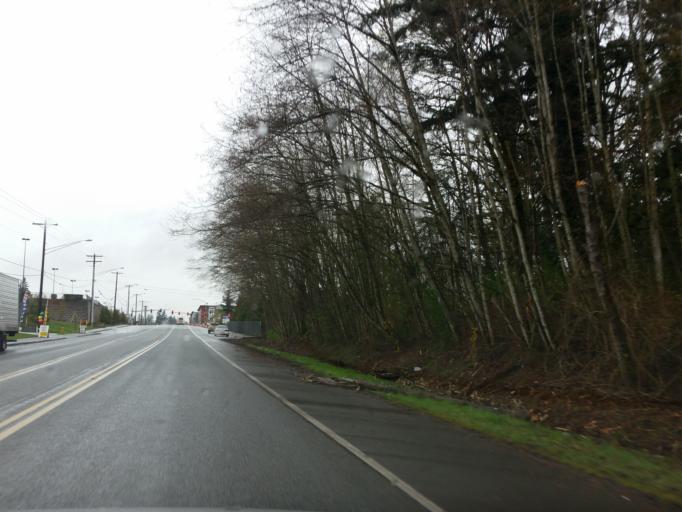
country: US
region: Washington
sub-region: Snohomish County
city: Alderwood Manor
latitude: 47.8450
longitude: -122.2711
